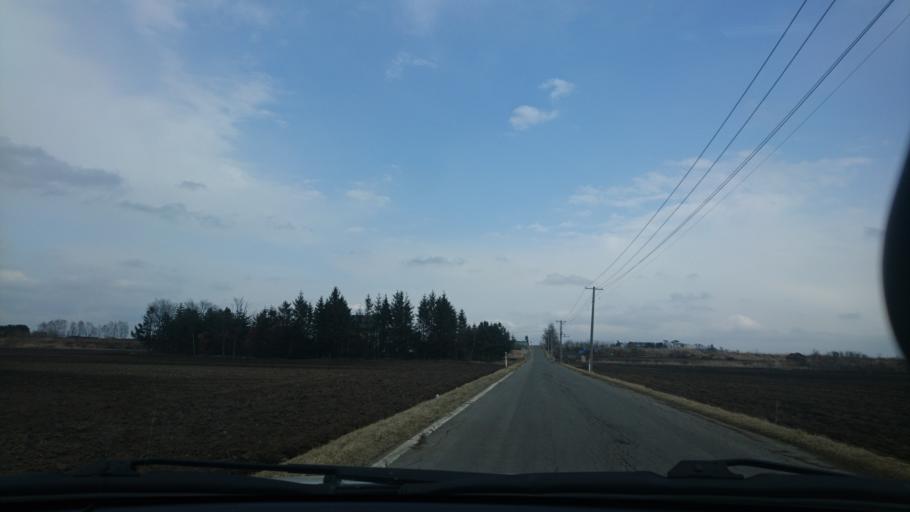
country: JP
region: Hokkaido
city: Otofuke
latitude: 43.0328
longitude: 143.2063
